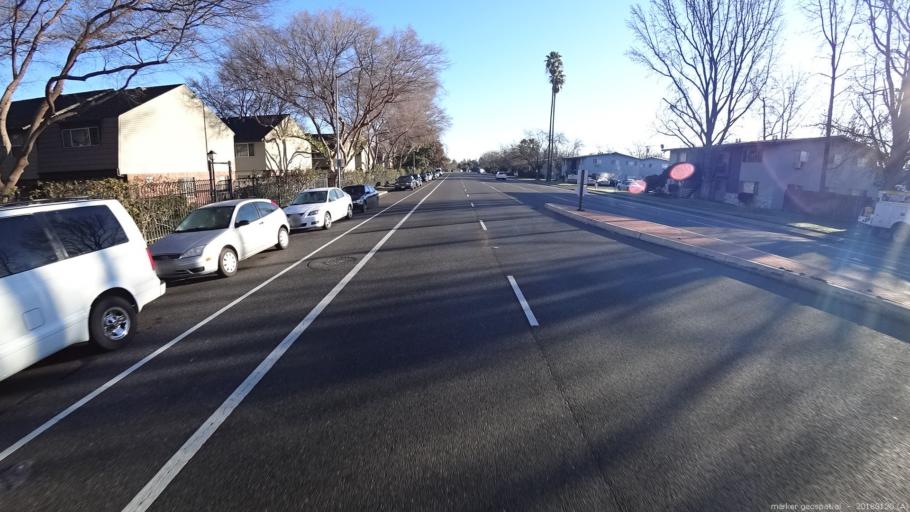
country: US
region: California
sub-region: Sacramento County
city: Fair Oaks
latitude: 38.6157
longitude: -121.2836
